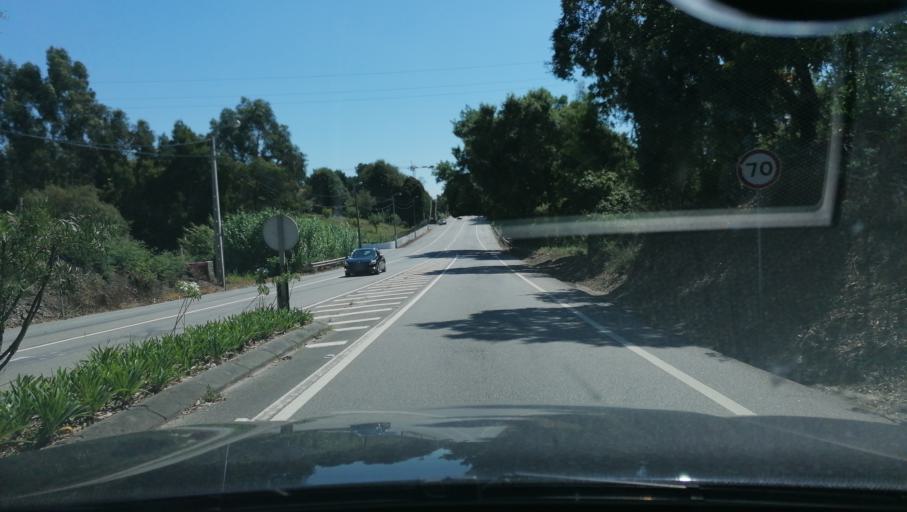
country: PT
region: Porto
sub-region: Vila Nova de Gaia
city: Gulpilhares
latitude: 41.0823
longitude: -8.6351
